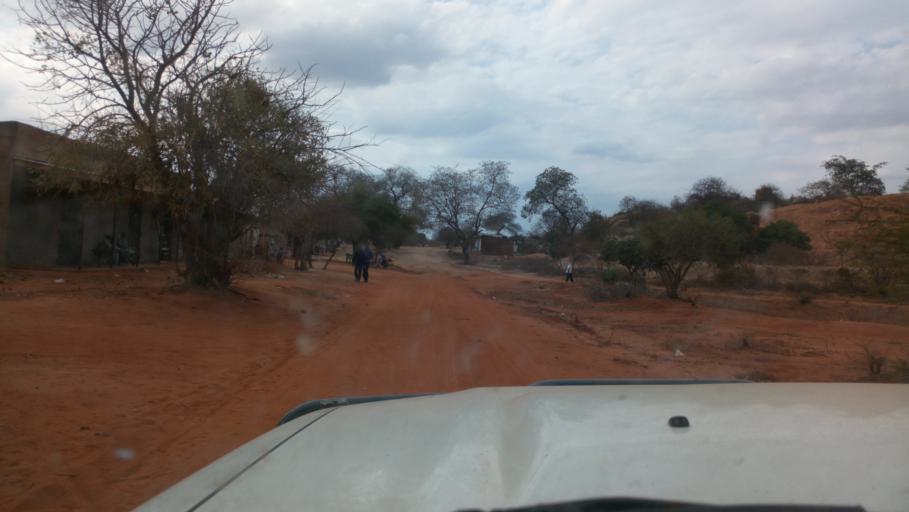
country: KE
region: Kitui
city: Kitui
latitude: -1.7514
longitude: 38.4407
